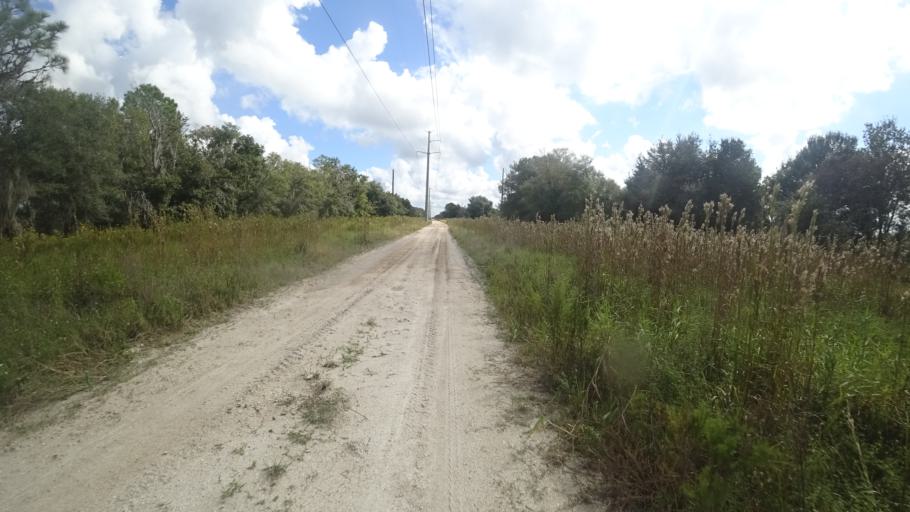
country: US
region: Florida
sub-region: Hillsborough County
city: Wimauma
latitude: 27.5162
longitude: -82.1261
